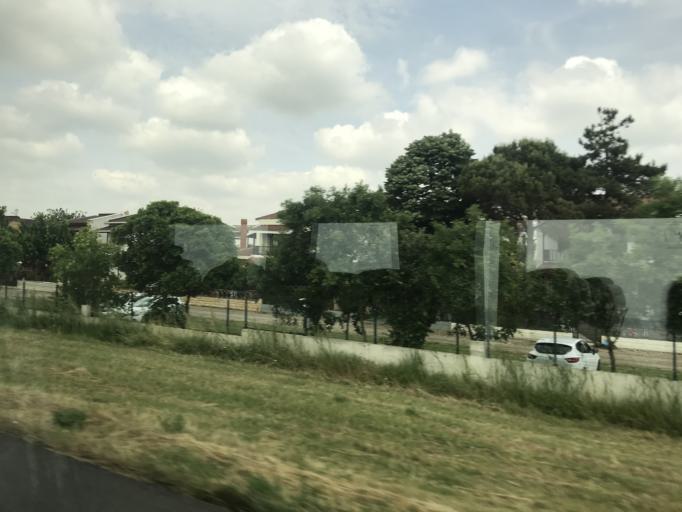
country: TR
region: Tekirdag
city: Corlu
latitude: 41.0130
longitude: 27.7342
